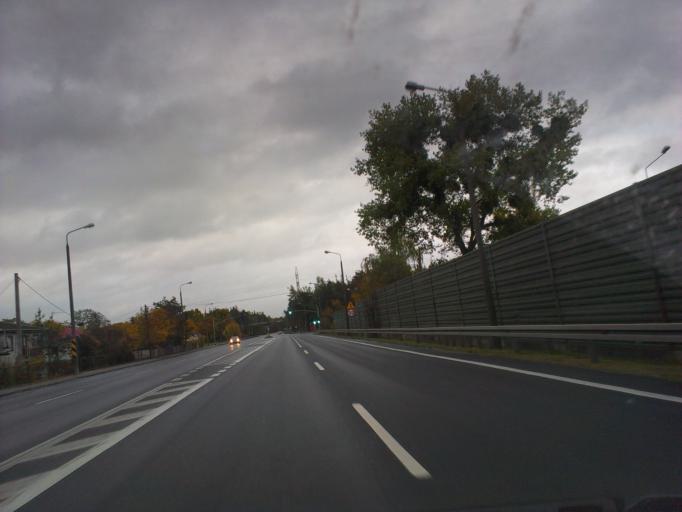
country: PL
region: Kujawsko-Pomorskie
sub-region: Powiat swiecki
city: Swiecie
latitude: 53.4054
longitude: 18.3915
